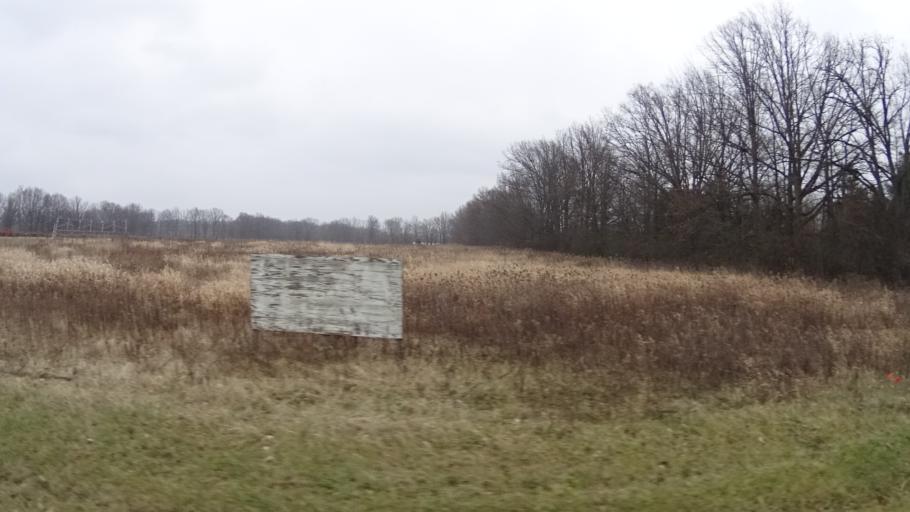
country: US
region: Ohio
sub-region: Lorain County
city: Oberlin
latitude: 41.2851
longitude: -82.1975
